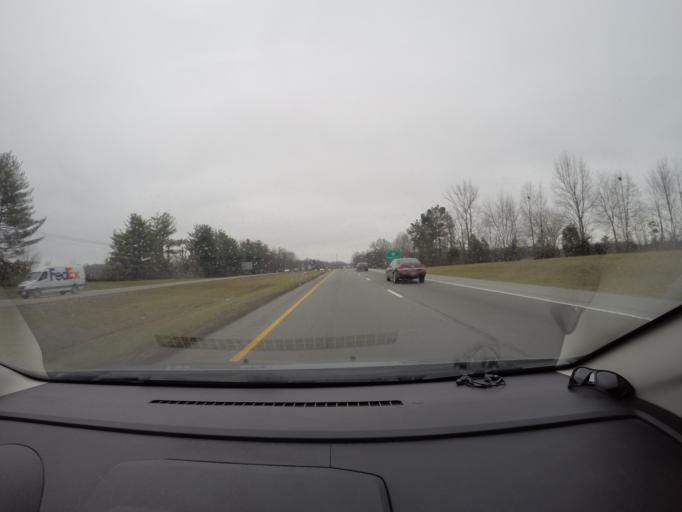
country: US
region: Tennessee
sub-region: Coffee County
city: Manchester
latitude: 35.4742
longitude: -86.0614
